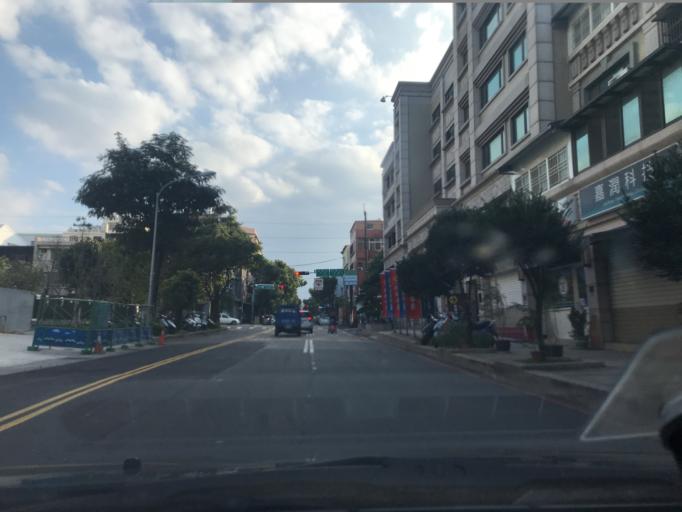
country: TW
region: Taiwan
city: Taoyuan City
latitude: 24.9785
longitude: 121.2346
